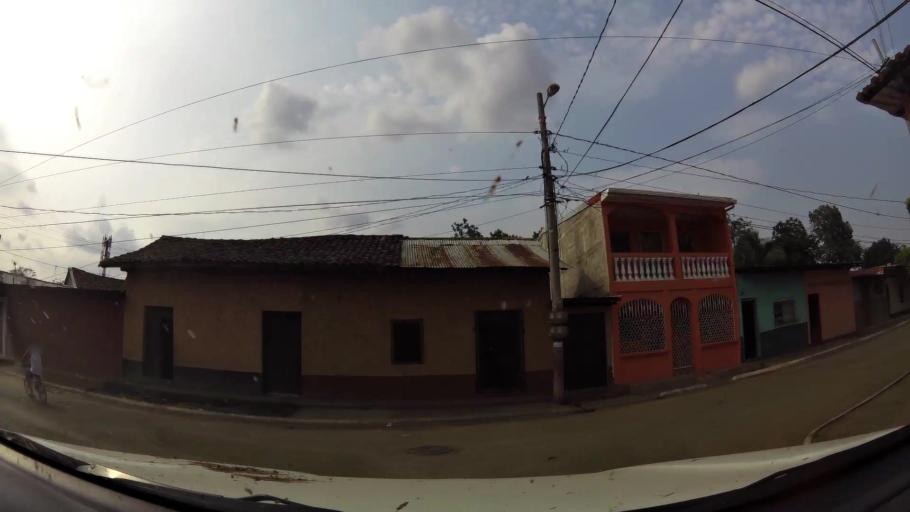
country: NI
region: Masaya
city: Masaya
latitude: 11.9701
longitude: -86.0924
